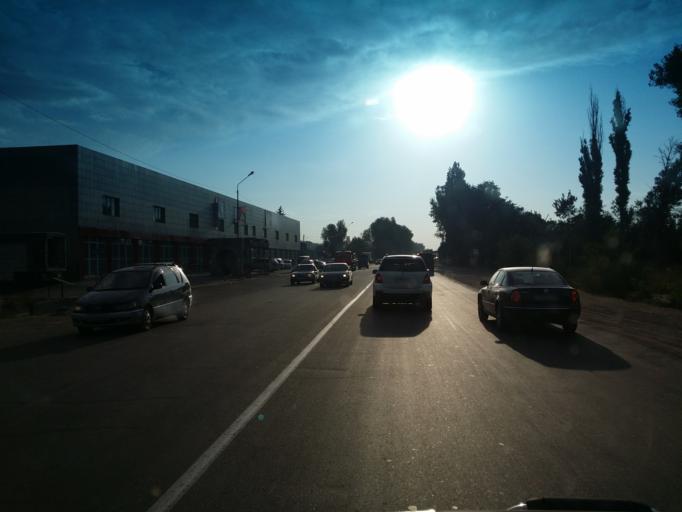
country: KZ
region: Almaty Oblysy
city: Talghar
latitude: 43.4047
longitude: 77.2198
